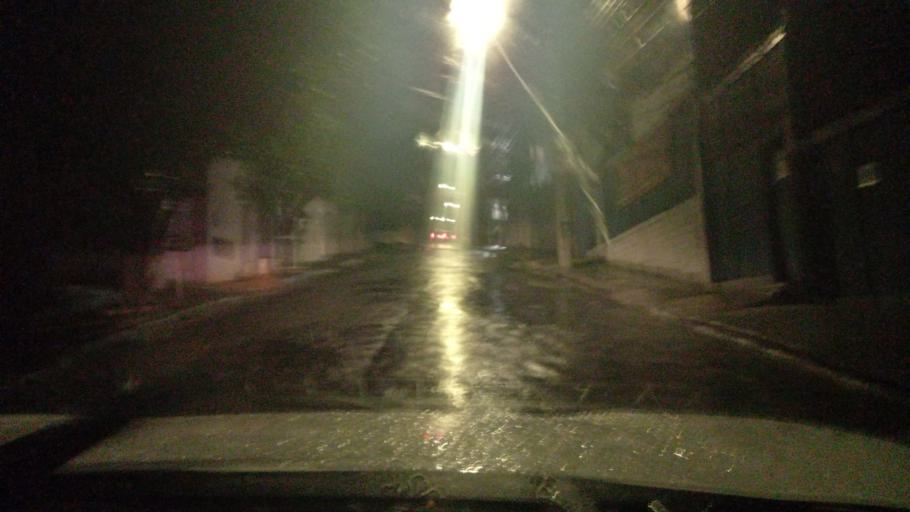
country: BR
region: Minas Gerais
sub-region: Belo Horizonte
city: Belo Horizonte
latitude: -19.9139
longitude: -43.9189
